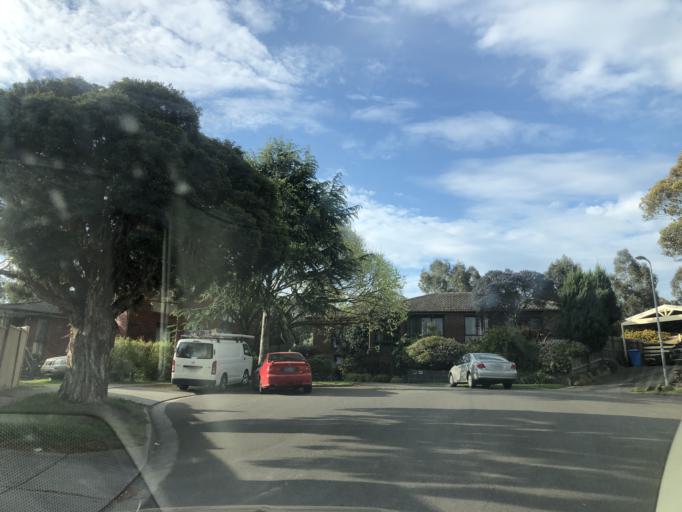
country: AU
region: Victoria
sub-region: Casey
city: Hallam
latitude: -38.0247
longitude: 145.2655
